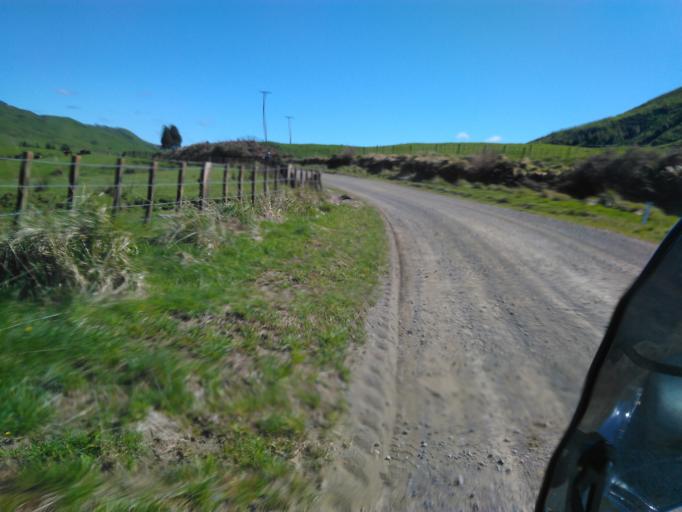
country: NZ
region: Bay of Plenty
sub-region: Opotiki District
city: Opotiki
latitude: -38.3098
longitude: 177.5643
